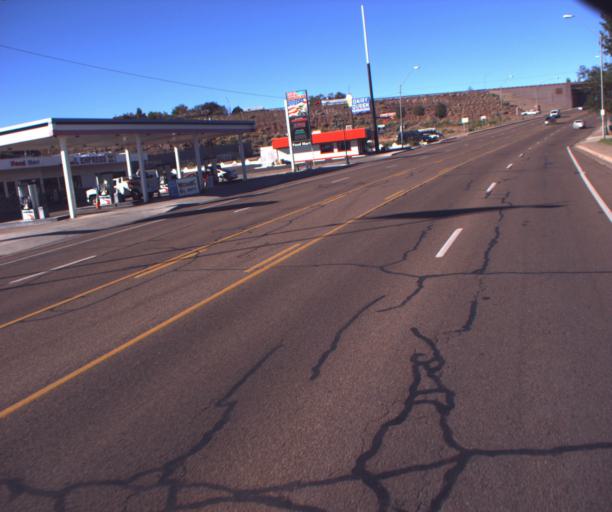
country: US
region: Arizona
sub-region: Navajo County
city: Holbrook
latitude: 34.9098
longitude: -110.1579
